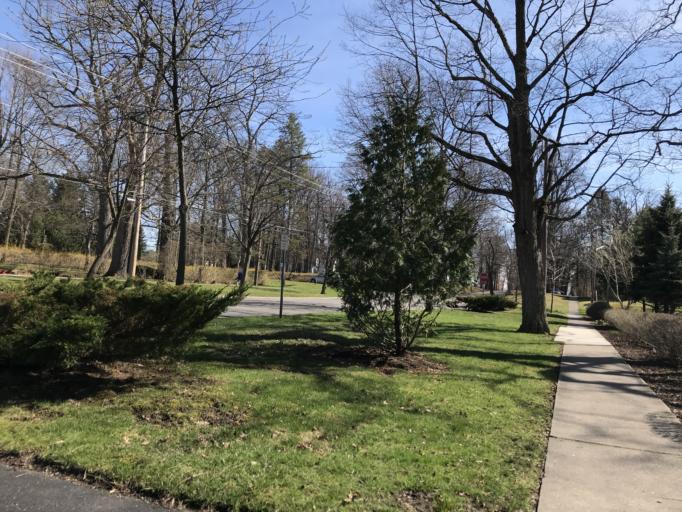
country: US
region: New York
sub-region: Livingston County
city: Geneseo
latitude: 42.7958
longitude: -77.8076
